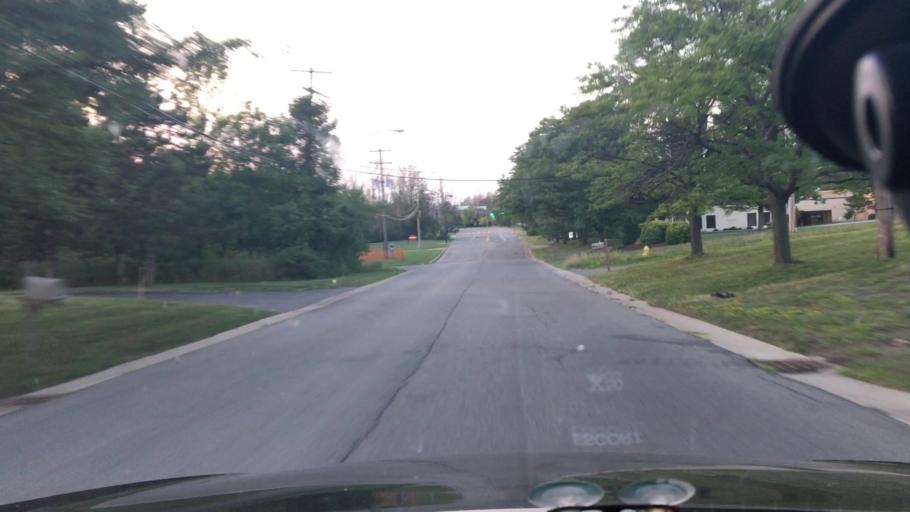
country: US
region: New York
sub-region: Erie County
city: Orchard Park
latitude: 42.7867
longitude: -78.7665
